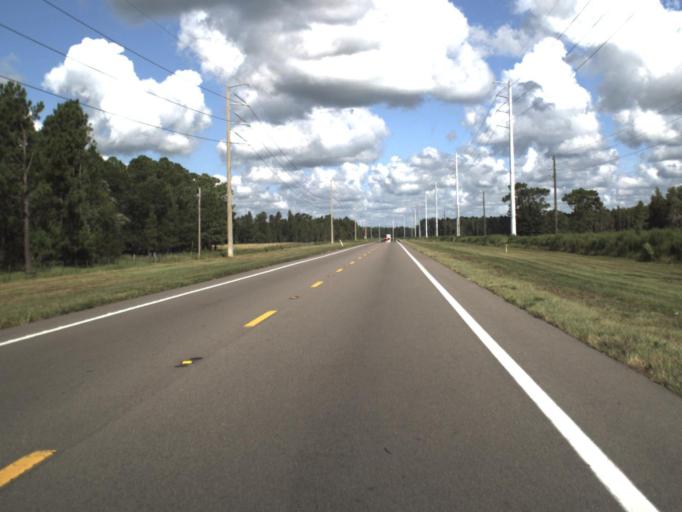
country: US
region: Florida
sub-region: Polk County
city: Kathleen
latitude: 28.2354
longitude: -82.0405
